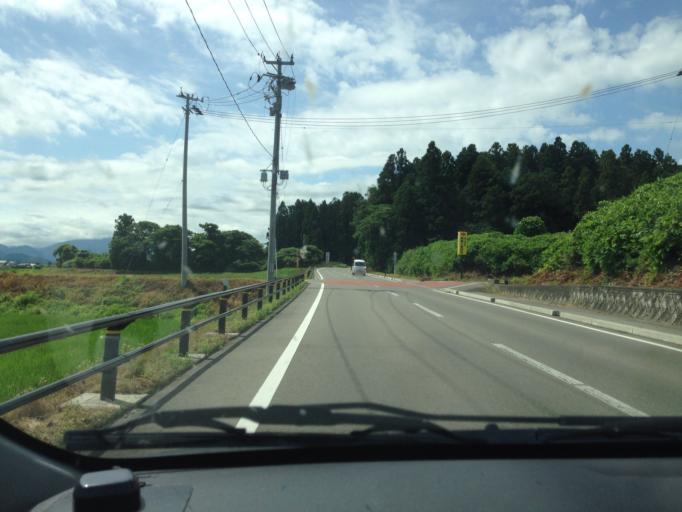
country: JP
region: Fukushima
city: Kitakata
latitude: 37.5234
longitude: 139.8347
